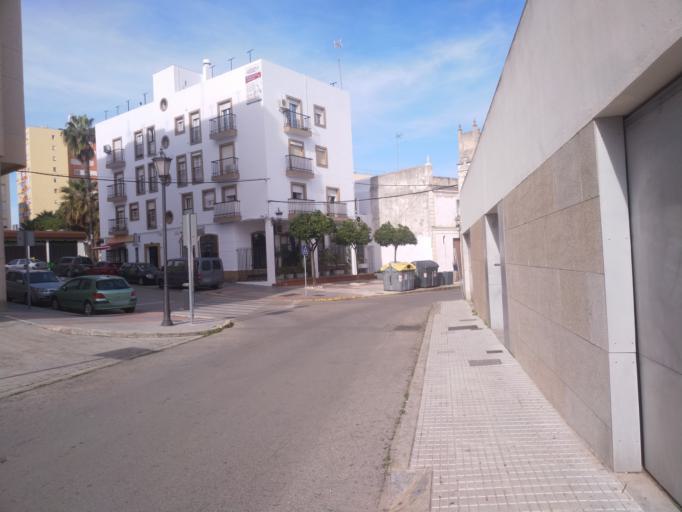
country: ES
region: Andalusia
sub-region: Provincia de Cadiz
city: San Fernando
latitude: 36.4677
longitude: -6.1981
